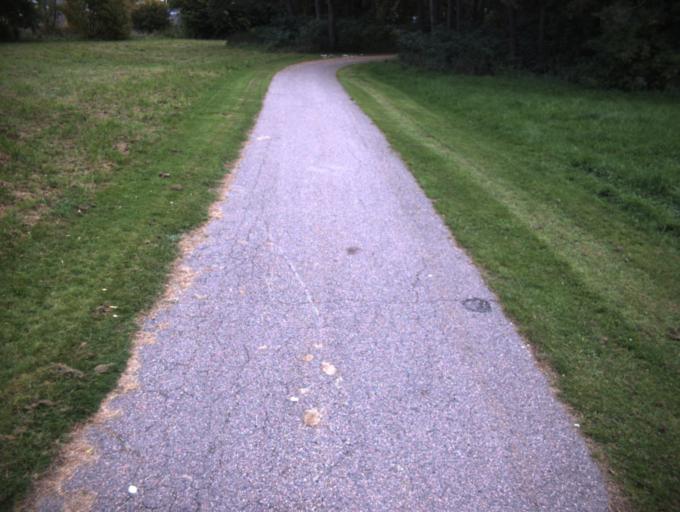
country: SE
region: Skane
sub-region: Helsingborg
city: Odakra
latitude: 56.0743
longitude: 12.7222
